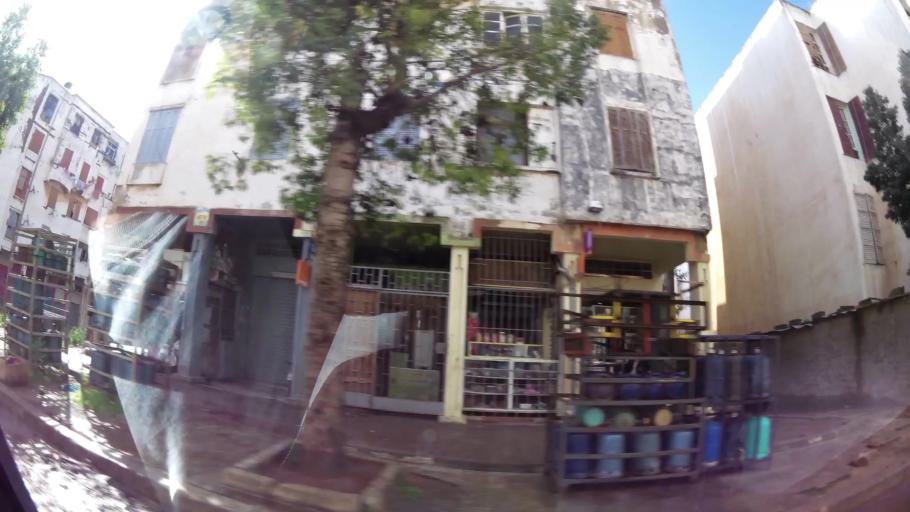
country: MA
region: Grand Casablanca
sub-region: Mediouna
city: Tit Mellil
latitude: 33.5766
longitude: -7.5232
